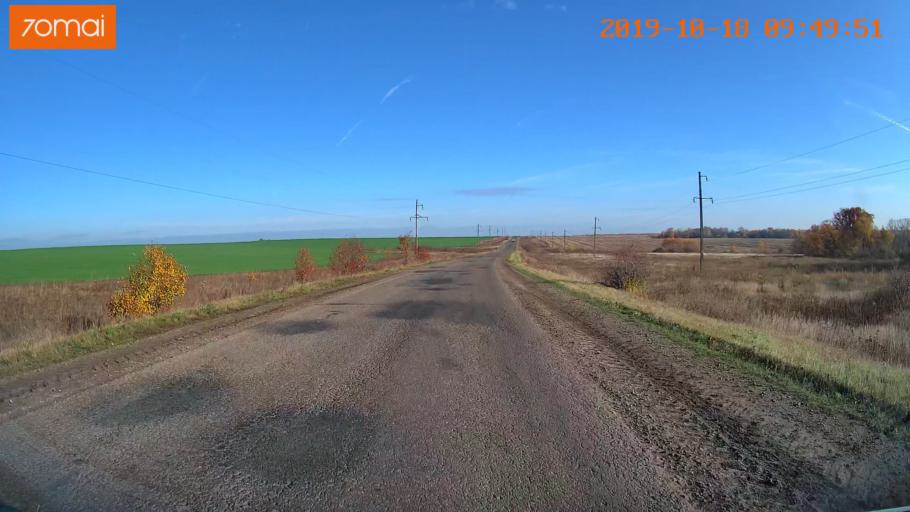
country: RU
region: Tula
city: Kazachka
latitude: 53.3224
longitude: 38.2697
